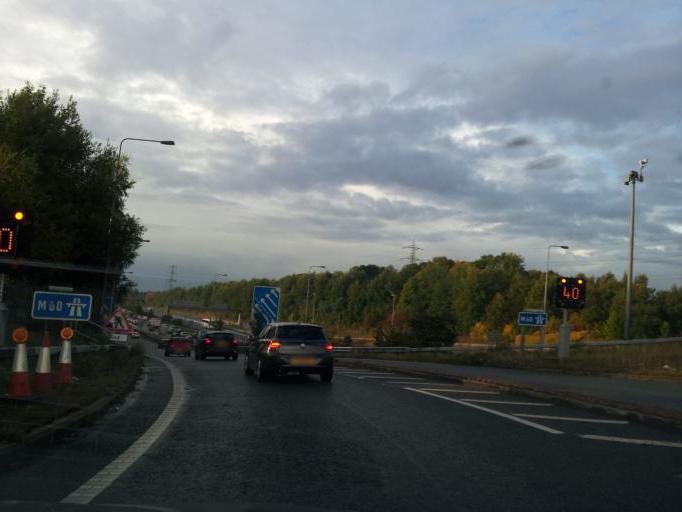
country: GB
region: England
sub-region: Manchester
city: Crumpsall
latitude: 53.5396
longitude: -2.2385
